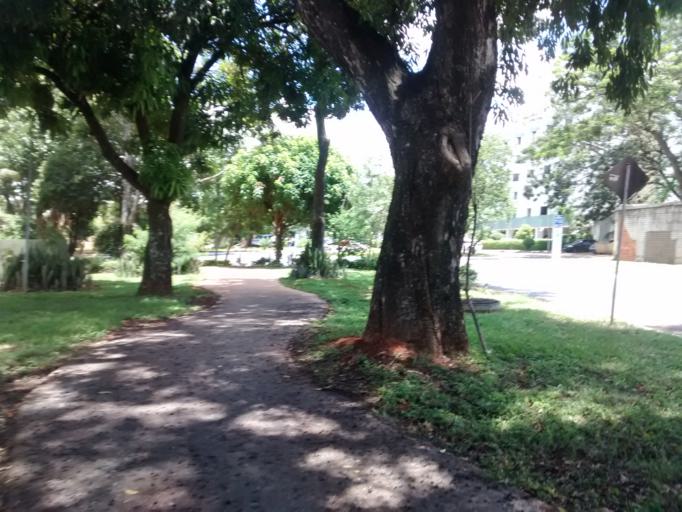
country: BR
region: Federal District
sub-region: Brasilia
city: Brasilia
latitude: -15.8182
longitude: -47.9187
